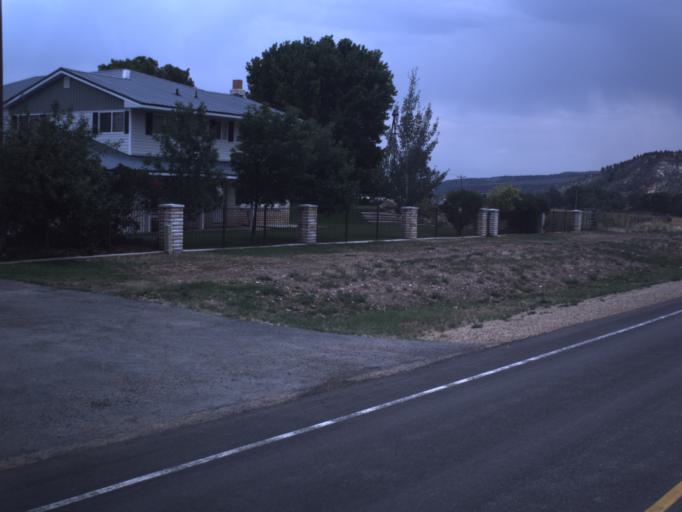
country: US
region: Utah
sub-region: Duchesne County
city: Duchesne
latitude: 40.4273
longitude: -110.8018
